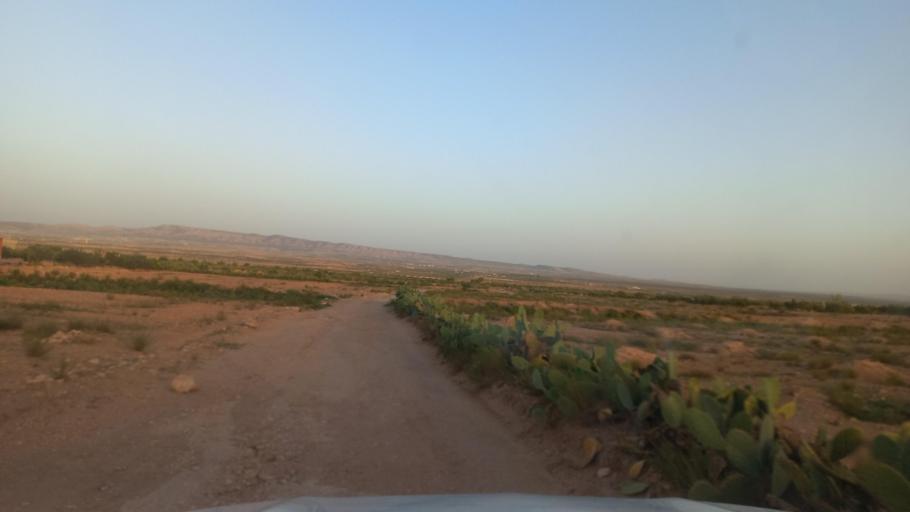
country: TN
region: Al Qasrayn
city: Sbiba
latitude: 35.3743
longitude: 9.0108
